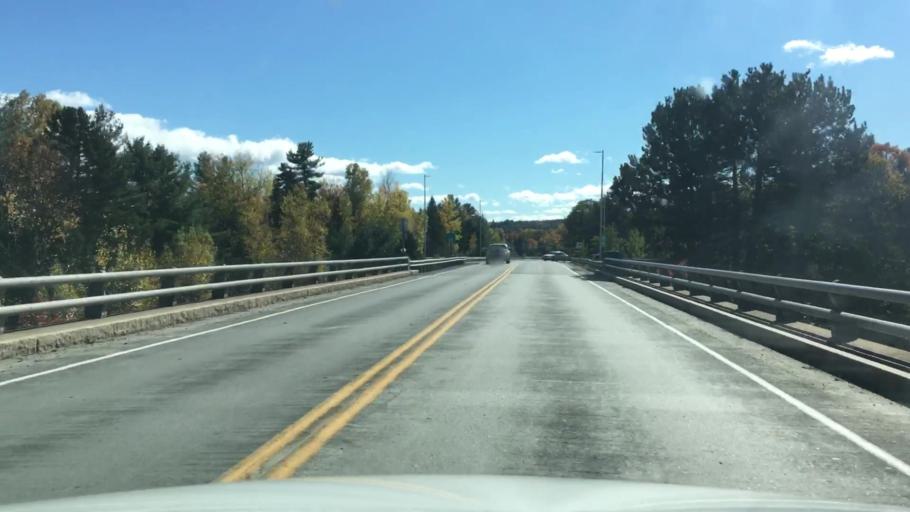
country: US
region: Maine
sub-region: Penobscot County
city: Medway
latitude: 45.6069
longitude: -68.5221
